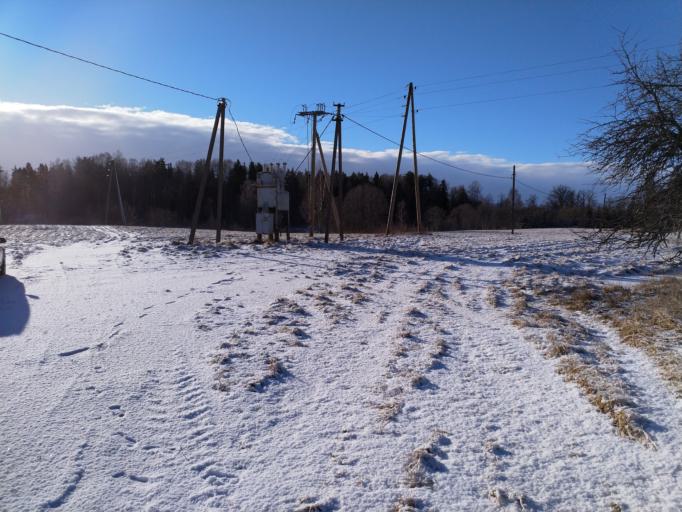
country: LV
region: Aizpute
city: Aizpute
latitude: 56.6592
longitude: 21.6434
